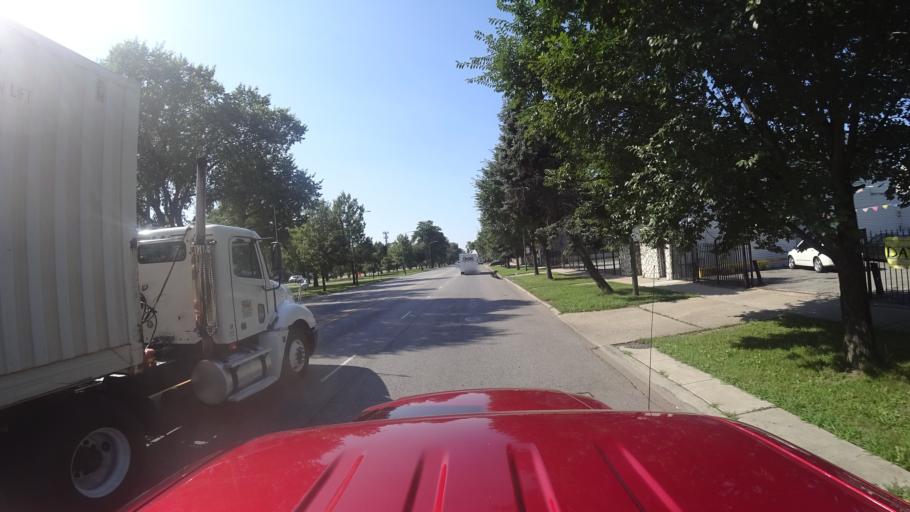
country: US
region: Illinois
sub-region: Cook County
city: Chicago
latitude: 41.8004
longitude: -87.6843
